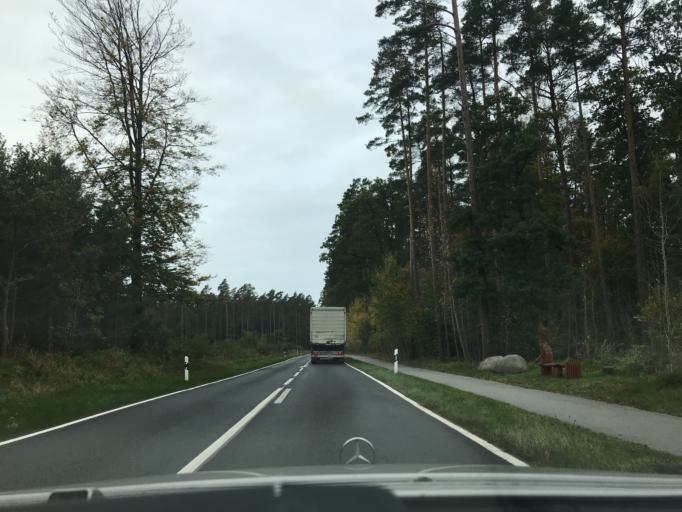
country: DE
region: Mecklenburg-Vorpommern
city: Kroslin
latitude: 54.1383
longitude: 13.7105
